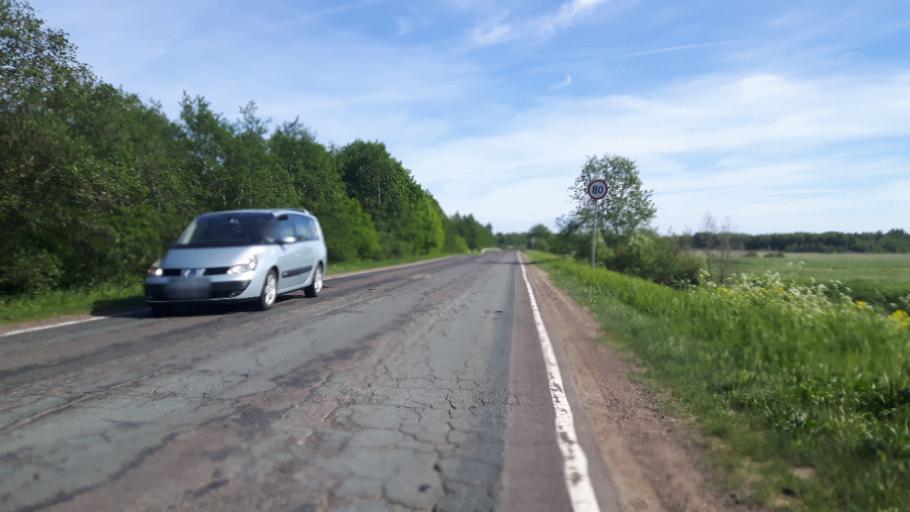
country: RU
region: Leningrad
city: Ivangorod
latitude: 59.4182
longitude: 28.3237
